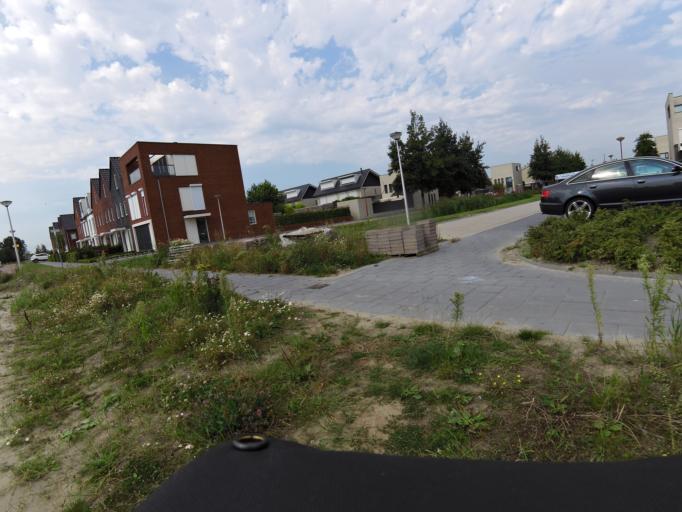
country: NL
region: South Holland
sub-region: Gemeente Oud-Beijerland
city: Oud-Beijerland
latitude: 51.8133
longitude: 4.4310
